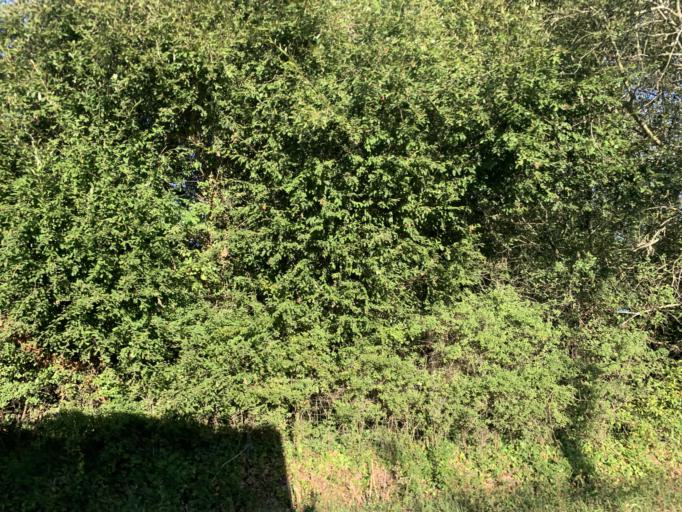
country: FR
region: Pays de la Loire
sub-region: Departement de la Loire-Atlantique
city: Pornichet
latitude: 47.2561
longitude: -2.3036
